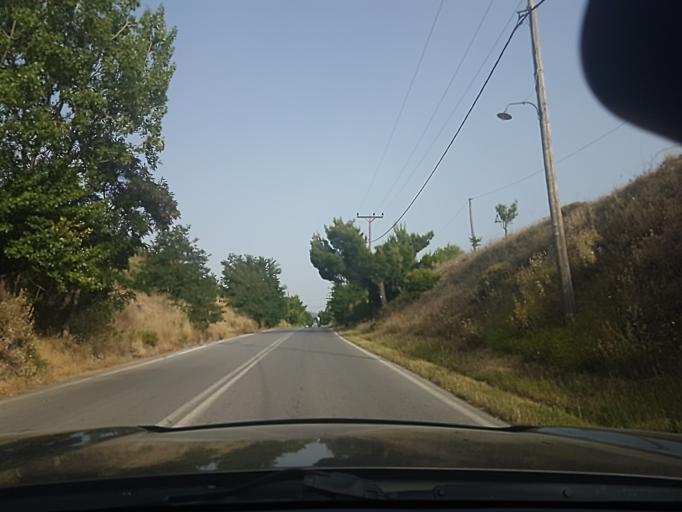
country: GR
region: Central Greece
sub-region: Nomos Evvoias
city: Yimnon
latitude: 38.5753
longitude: 23.8183
